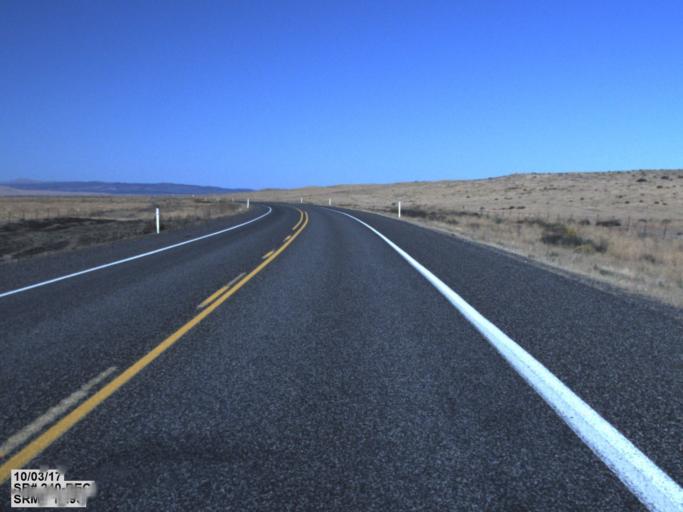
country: US
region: Washington
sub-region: Benton County
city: Benton City
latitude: 46.4452
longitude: -119.4958
